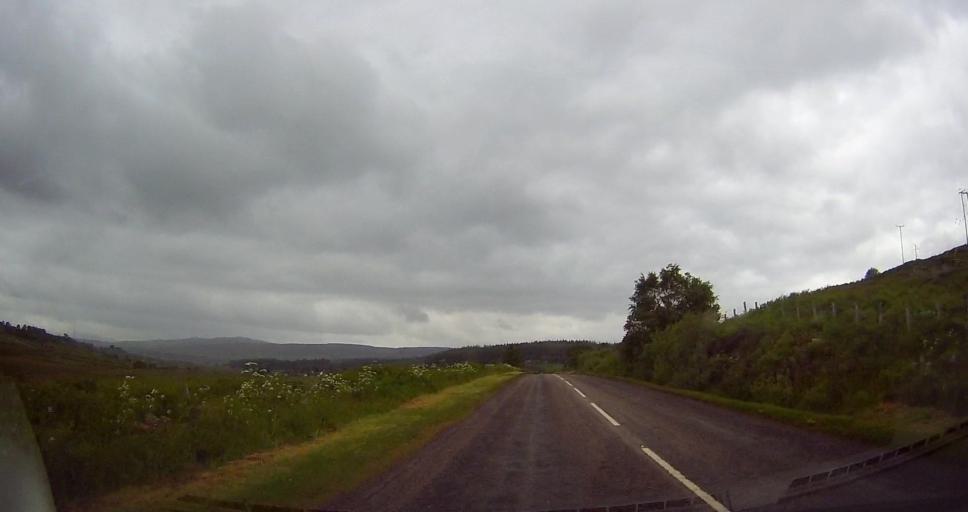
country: GB
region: Scotland
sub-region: Highland
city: Alness
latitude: 58.0182
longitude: -4.3612
